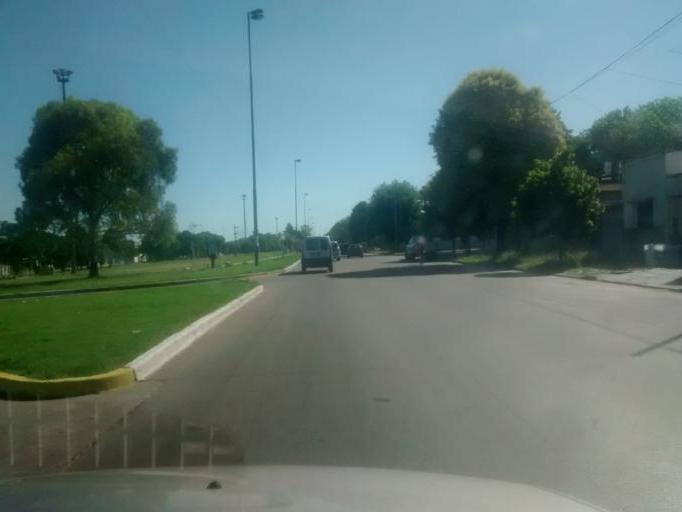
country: AR
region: Buenos Aires
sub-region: Partido de La Plata
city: La Plata
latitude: -34.9315
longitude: -57.9285
